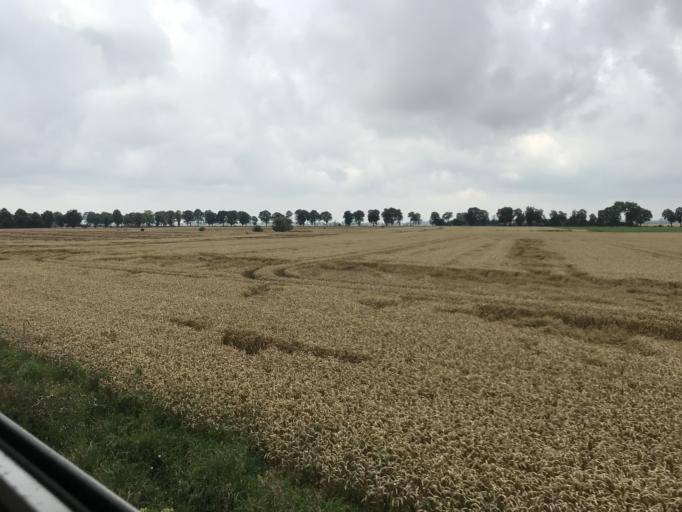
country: PL
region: Pomeranian Voivodeship
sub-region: Powiat malborski
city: Stare Pole
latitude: 54.0625
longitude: 19.2360
